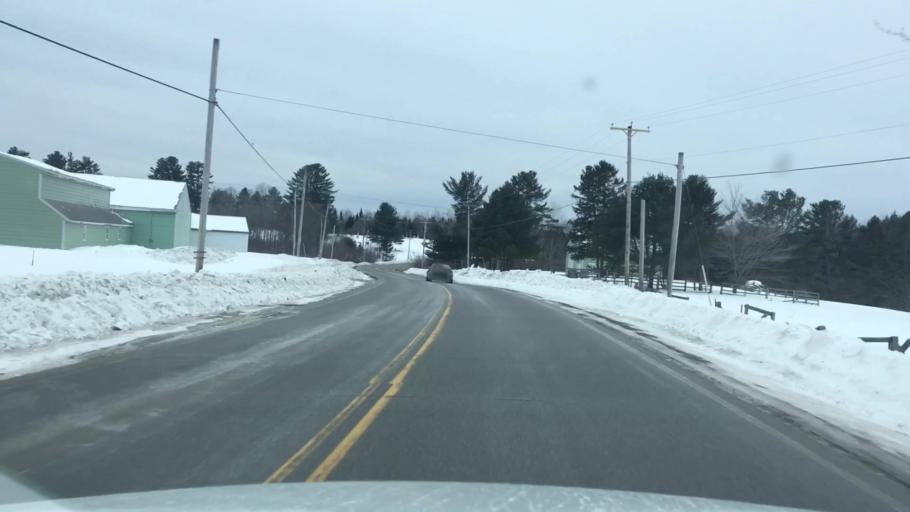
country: US
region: Maine
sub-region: Penobscot County
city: Charleston
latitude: 44.9988
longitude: -69.0356
